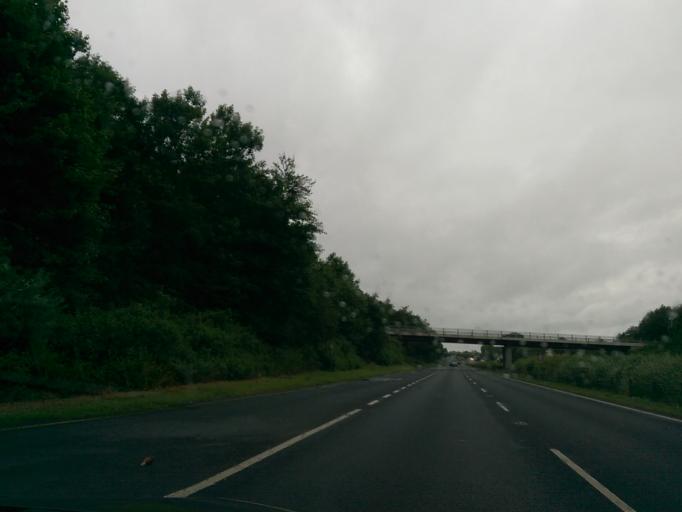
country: IE
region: Munster
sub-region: An Clar
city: Sixmilebridge
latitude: 52.6905
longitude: -8.7481
